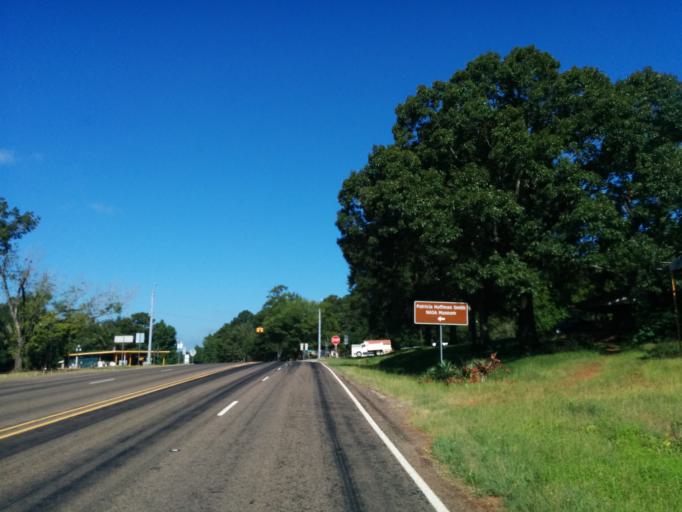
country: US
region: Texas
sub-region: Sabine County
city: Milam
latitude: 31.4329
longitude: -93.8454
